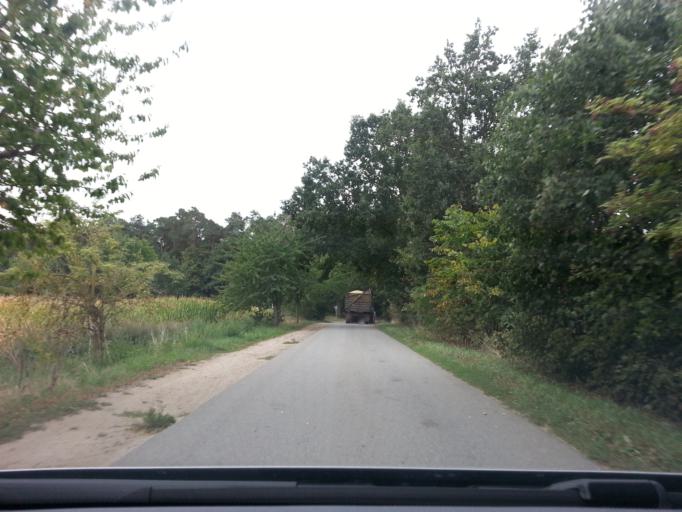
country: DE
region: Mecklenburg-Vorpommern
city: Ferdinandshof
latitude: 53.6595
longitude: 13.9180
